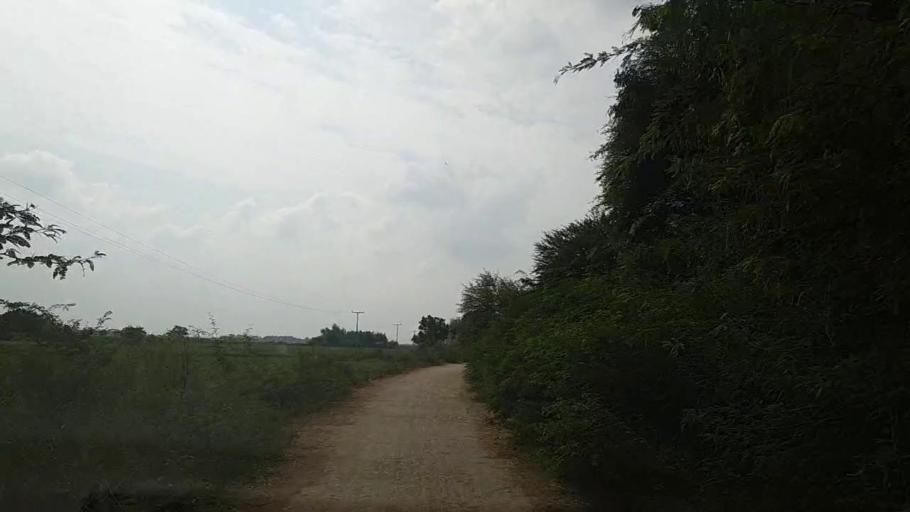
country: PK
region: Sindh
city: Mirpur Batoro
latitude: 24.5928
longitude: 68.1283
